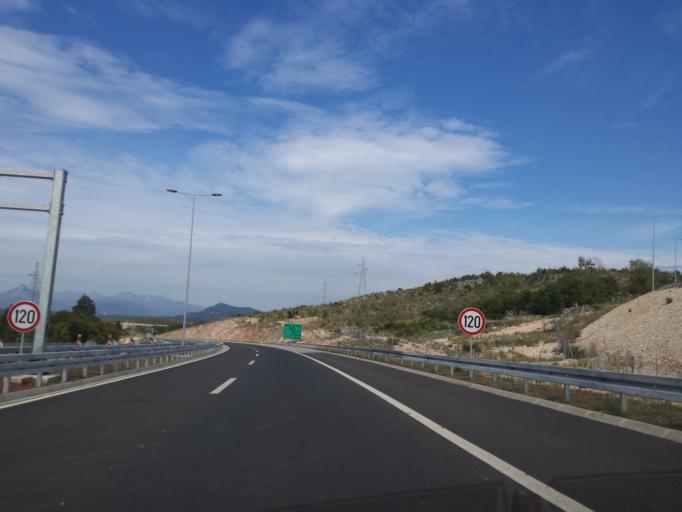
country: BA
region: Federation of Bosnia and Herzegovina
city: Capljina
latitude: 43.1600
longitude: 17.6569
